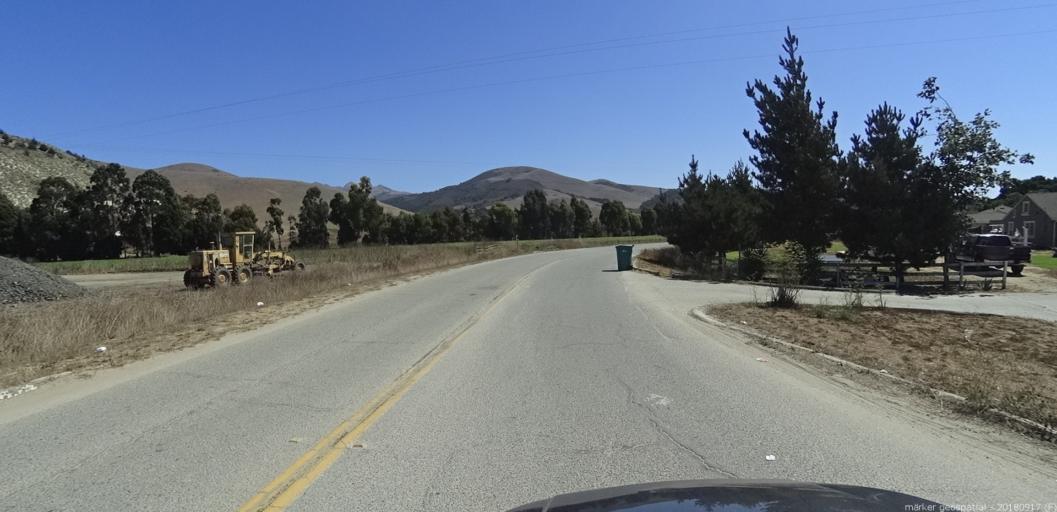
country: US
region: California
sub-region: Monterey County
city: Prunedale
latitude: 36.7400
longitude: -121.6020
